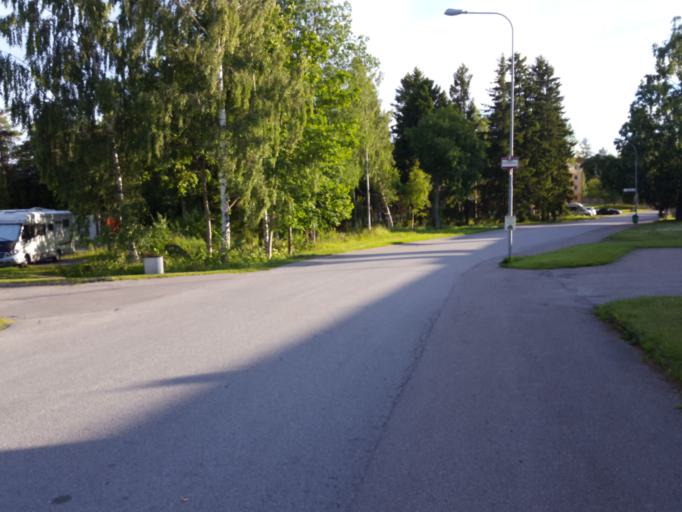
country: SE
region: Uppsala
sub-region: Osthammars Kommun
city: OEsthammar
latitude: 60.2568
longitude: 18.3549
